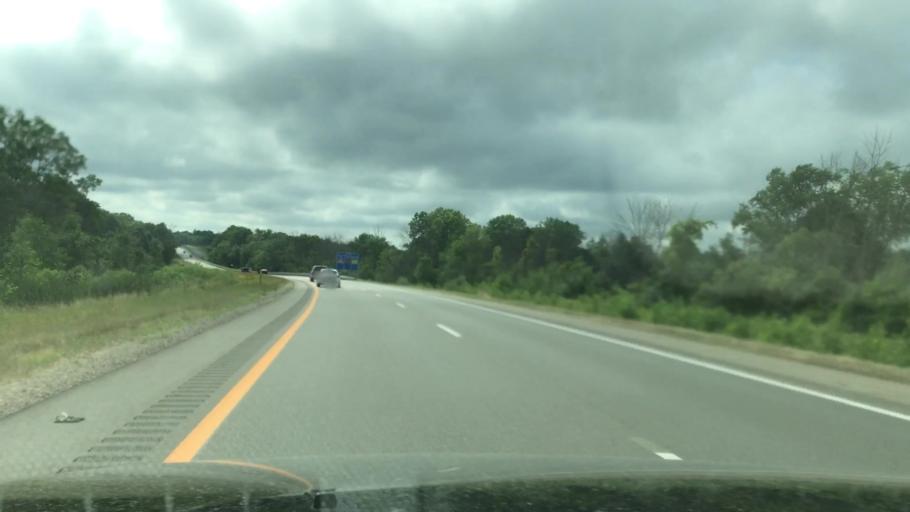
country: US
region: Michigan
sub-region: Ottawa County
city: Coopersville
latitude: 43.0741
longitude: -86.0439
